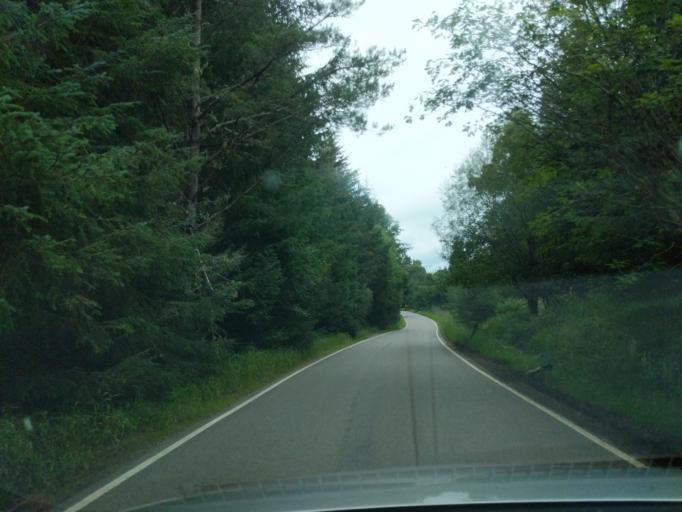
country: GB
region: Scotland
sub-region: Moray
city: Forres
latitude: 57.5113
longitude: -3.6964
